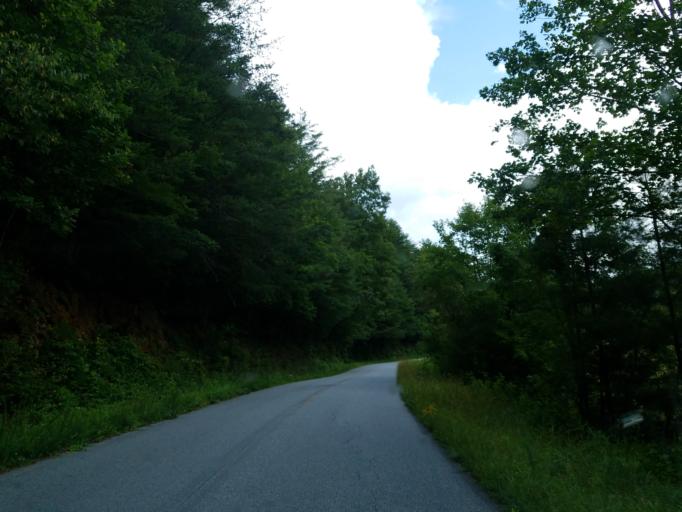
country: US
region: Georgia
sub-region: Fannin County
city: Blue Ridge
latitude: 34.7781
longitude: -84.3668
